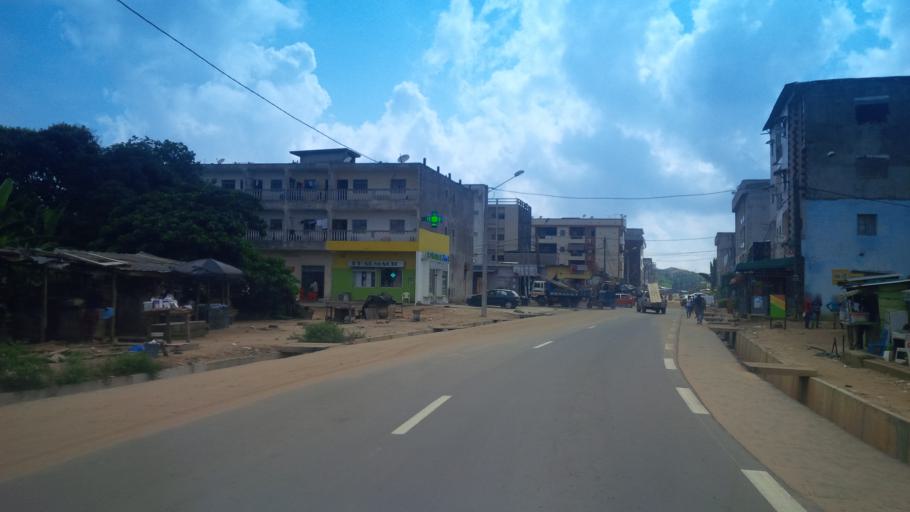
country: CI
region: Lagunes
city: Bingerville
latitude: 5.3786
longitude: -3.9537
